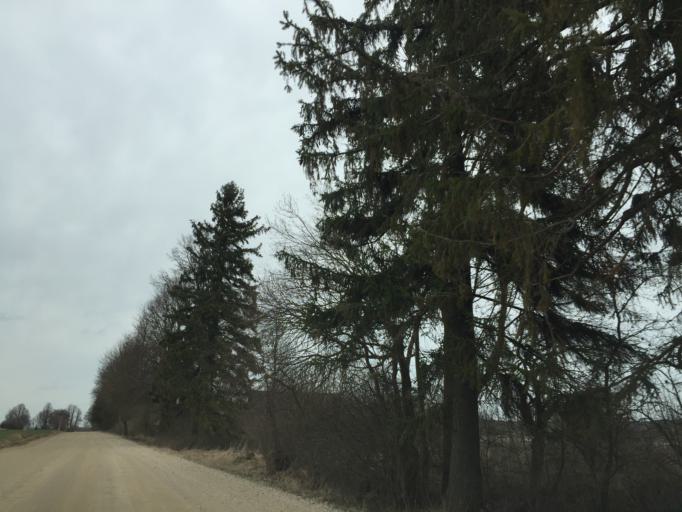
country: LV
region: Livani
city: Livani
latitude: 56.2920
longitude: 26.1754
